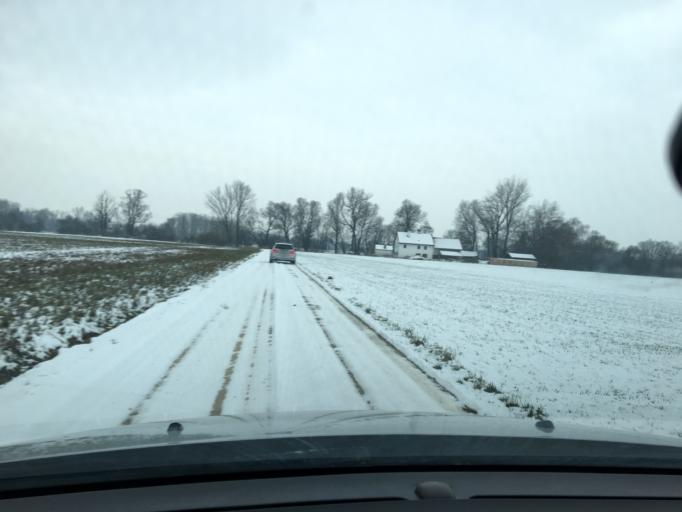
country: DE
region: Bavaria
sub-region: Upper Bavaria
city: Moosburg
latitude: 48.4633
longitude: 11.9039
